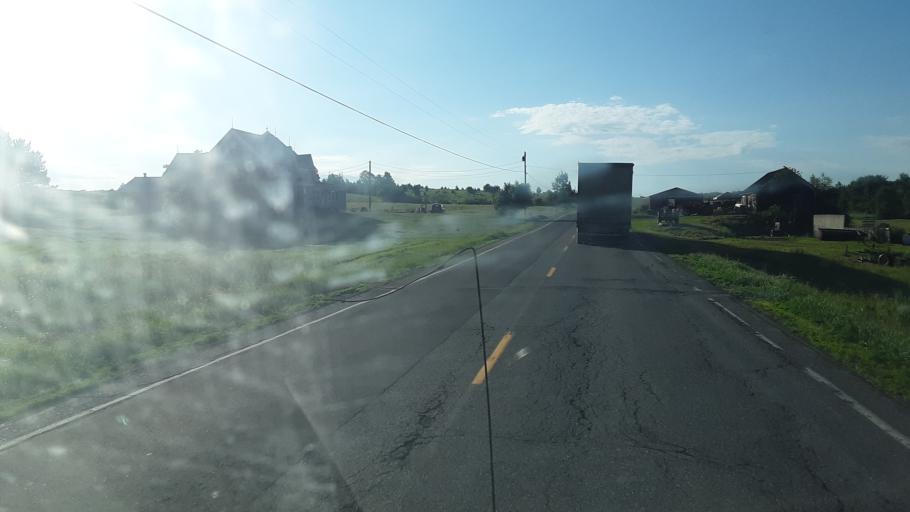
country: US
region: Maine
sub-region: Penobscot County
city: Patten
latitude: 46.1389
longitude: -68.1958
